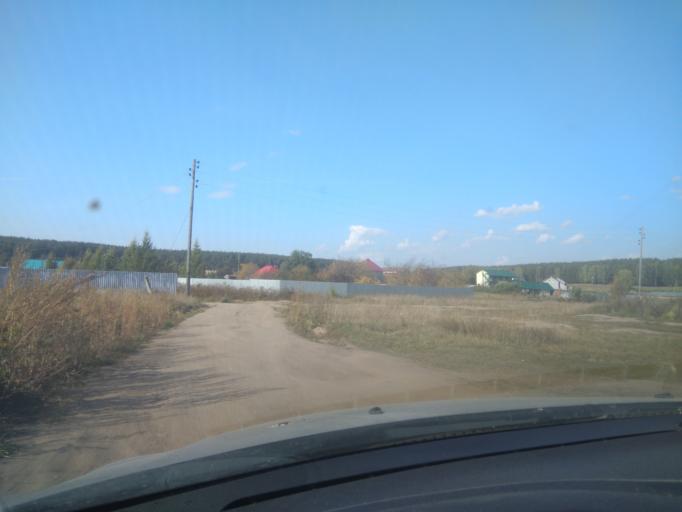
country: RU
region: Sverdlovsk
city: Pokrovskoye
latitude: 56.4355
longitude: 61.6018
